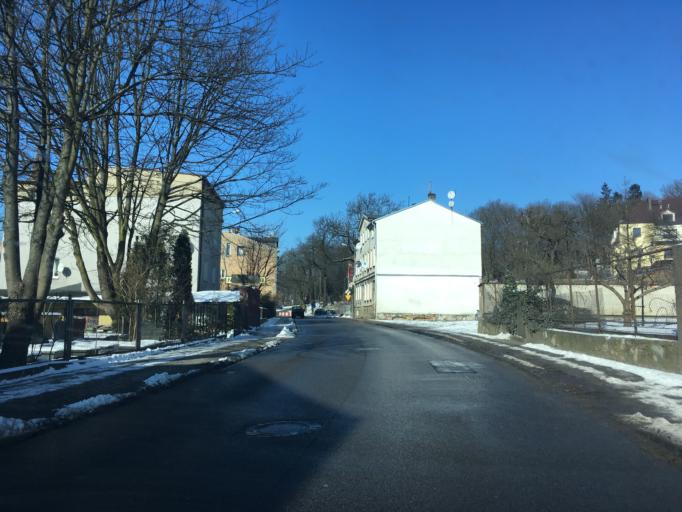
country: PL
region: Pomeranian Voivodeship
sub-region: Slupsk
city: Slupsk
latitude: 54.4678
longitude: 17.0425
